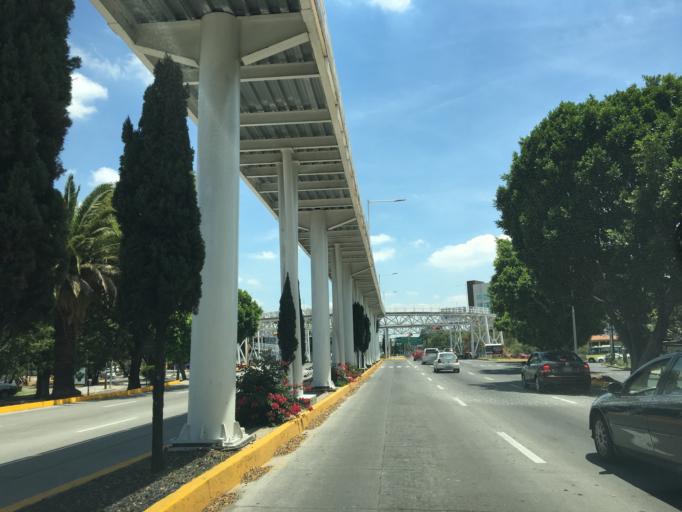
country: MX
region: Puebla
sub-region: Cuautlancingo
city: Sanctorum
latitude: 19.0897
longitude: -98.2293
